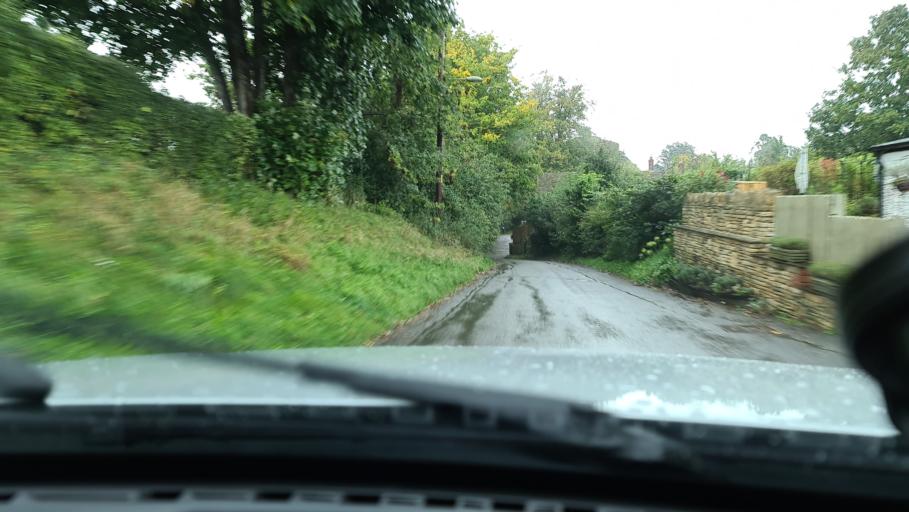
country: GB
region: England
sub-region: Oxfordshire
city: Deddington
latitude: 51.9263
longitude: -1.3683
